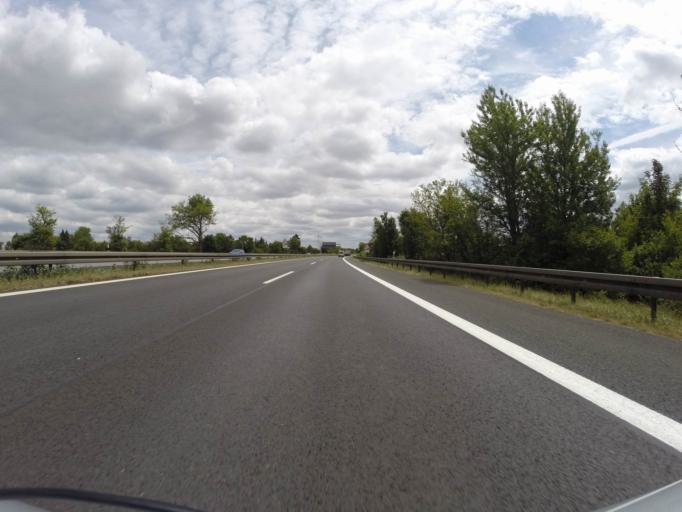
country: DE
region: Bavaria
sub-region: Regierungsbezirk Unterfranken
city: Bergrheinfeld
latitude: 50.0228
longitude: 10.1782
